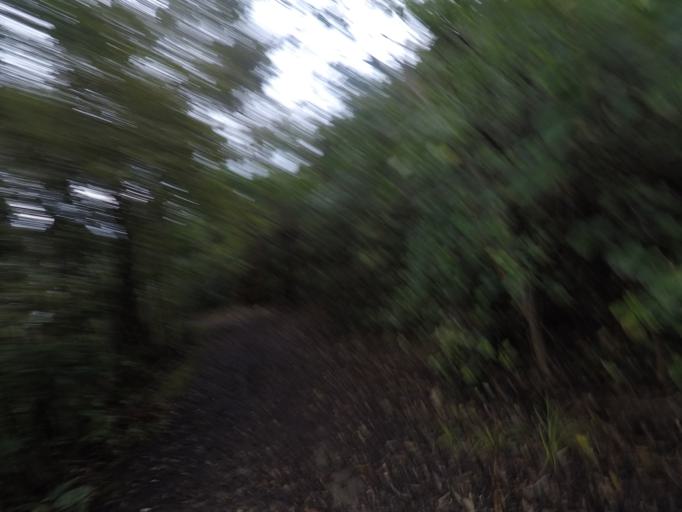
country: NZ
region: Bay of Plenty
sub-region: Western Bay of Plenty District
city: Waihi Beach
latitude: -37.3930
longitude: 175.9411
